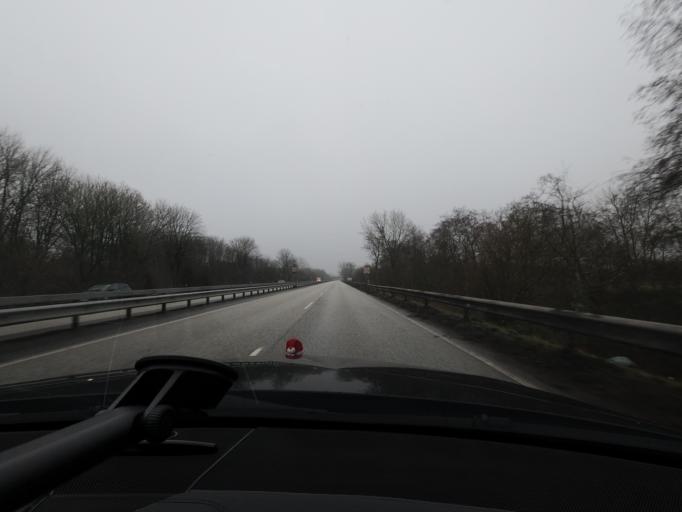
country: DE
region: Schleswig-Holstein
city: Flensburg
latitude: 54.7732
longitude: 9.4152
